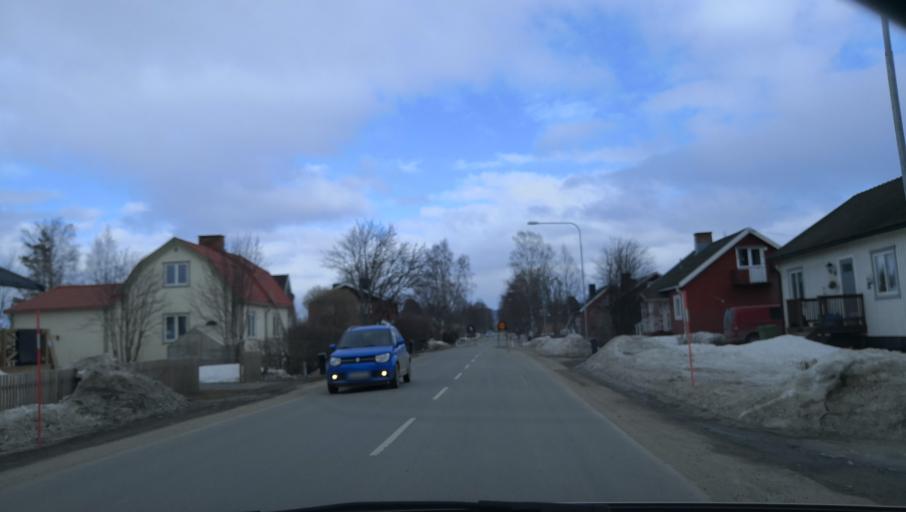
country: SE
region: Vaesterbotten
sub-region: Vannas Kommun
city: Vannasby
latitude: 63.9127
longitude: 19.8279
